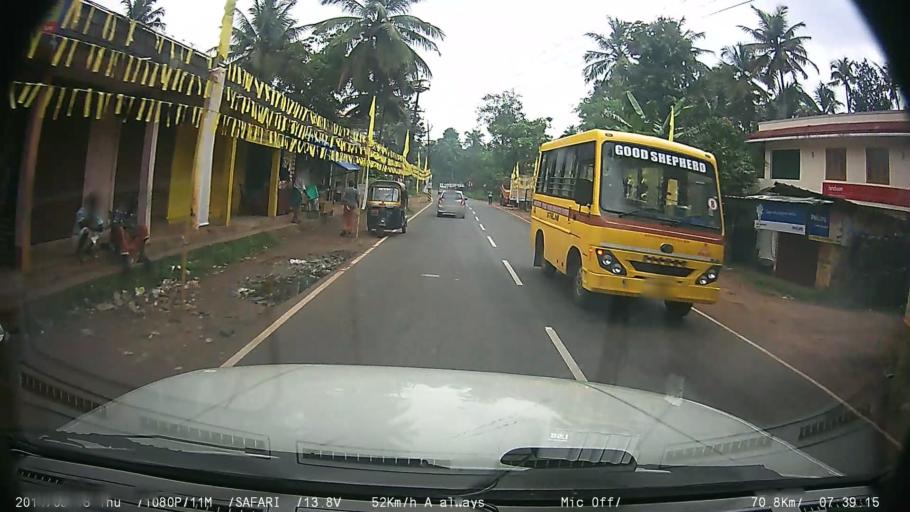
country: IN
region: Kerala
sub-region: Kottayam
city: Changanacheri
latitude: 9.4452
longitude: 76.5709
